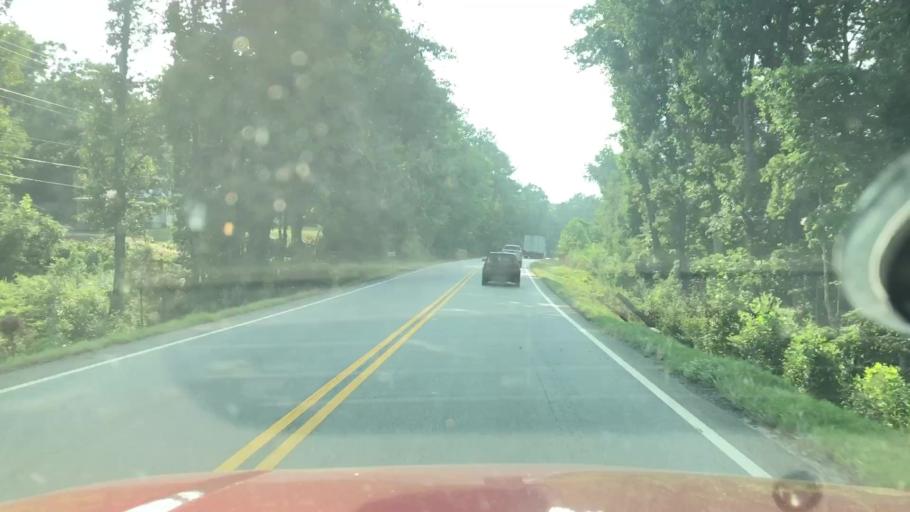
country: US
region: Georgia
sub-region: Bartow County
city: Cartersville
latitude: 34.0812
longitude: -84.8368
